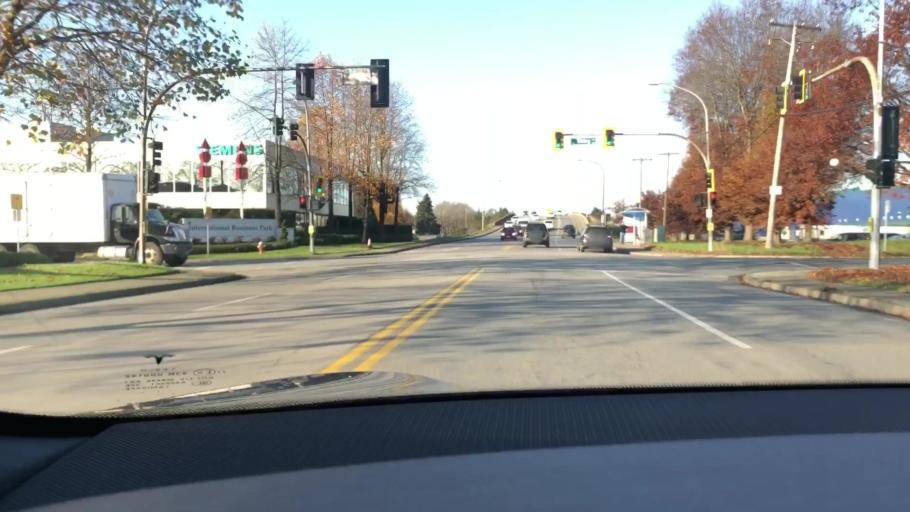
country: CA
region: British Columbia
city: Richmond
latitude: 49.1847
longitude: -123.0728
